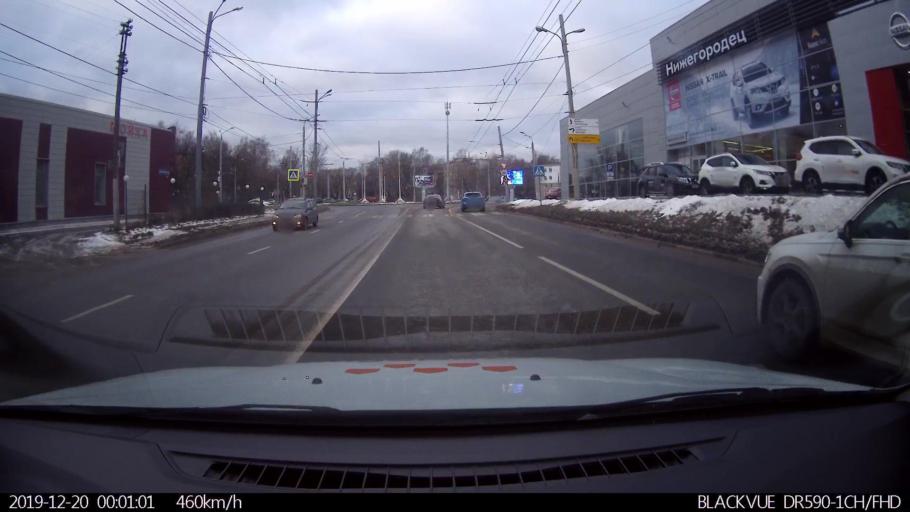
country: RU
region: Jaroslavl
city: Tutayev
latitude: 58.2407
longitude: 39.6521
